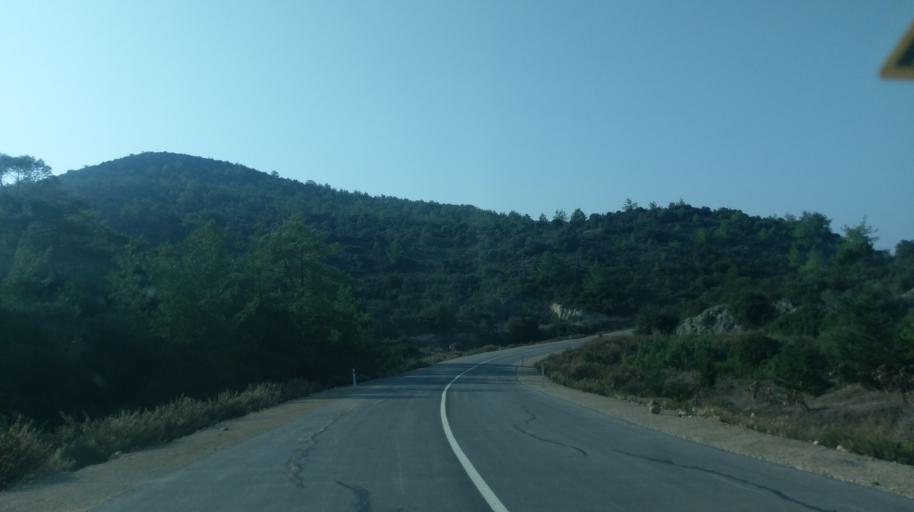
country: CY
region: Ammochostos
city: Leonarisso
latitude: 35.5330
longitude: 34.2462
